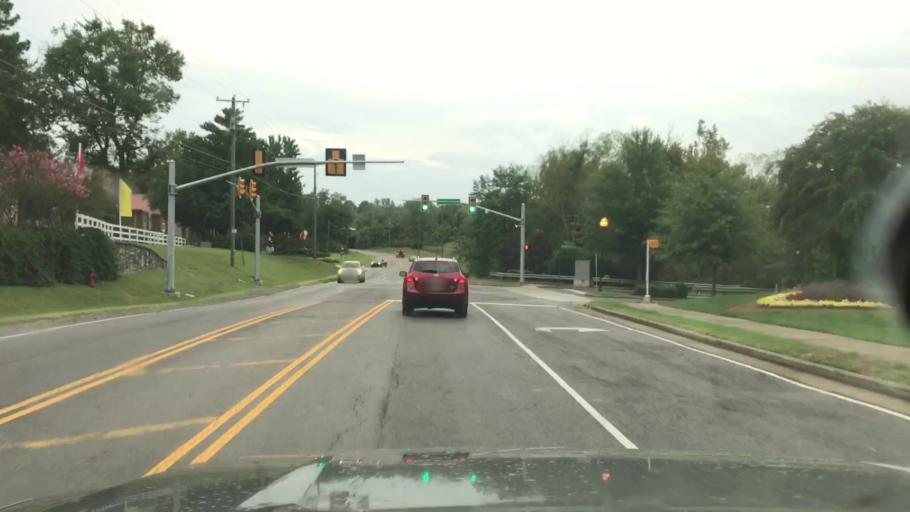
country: US
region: Tennessee
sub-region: Davidson County
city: Lakewood
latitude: 36.1685
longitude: -86.6150
